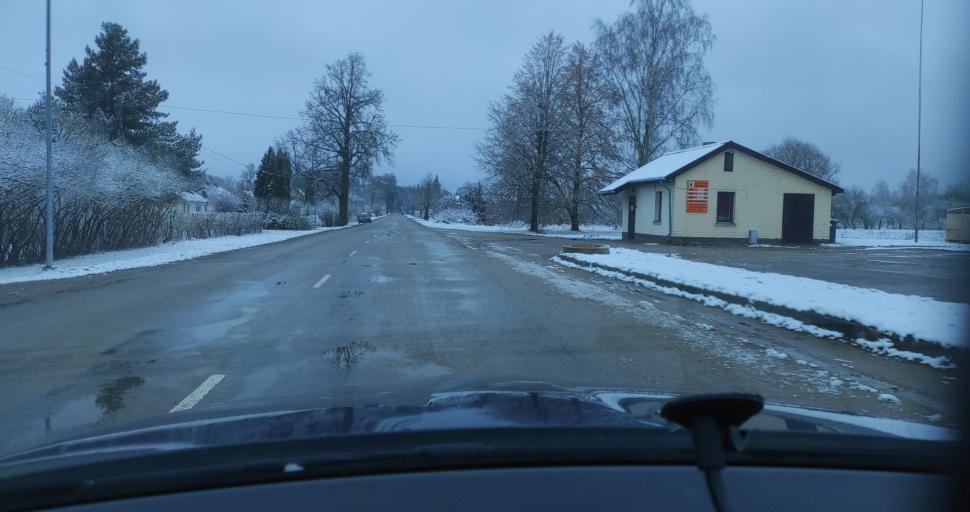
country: LV
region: Skrunda
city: Skrunda
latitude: 56.8681
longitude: 22.2331
